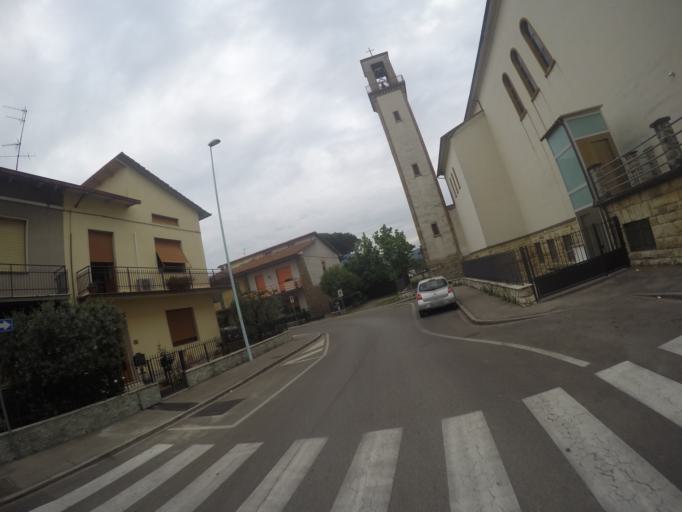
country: IT
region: Tuscany
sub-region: Provincia di Prato
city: Prato
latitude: 43.8959
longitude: 11.0659
